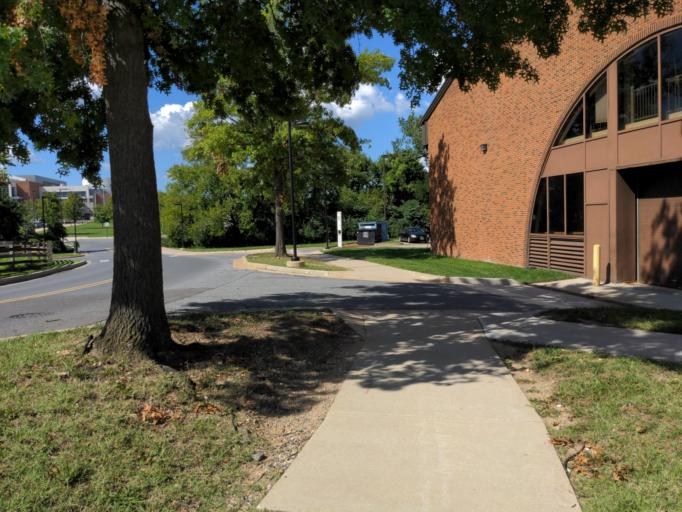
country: US
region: Maryland
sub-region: Prince George's County
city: College Park
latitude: 38.9928
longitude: -76.9398
